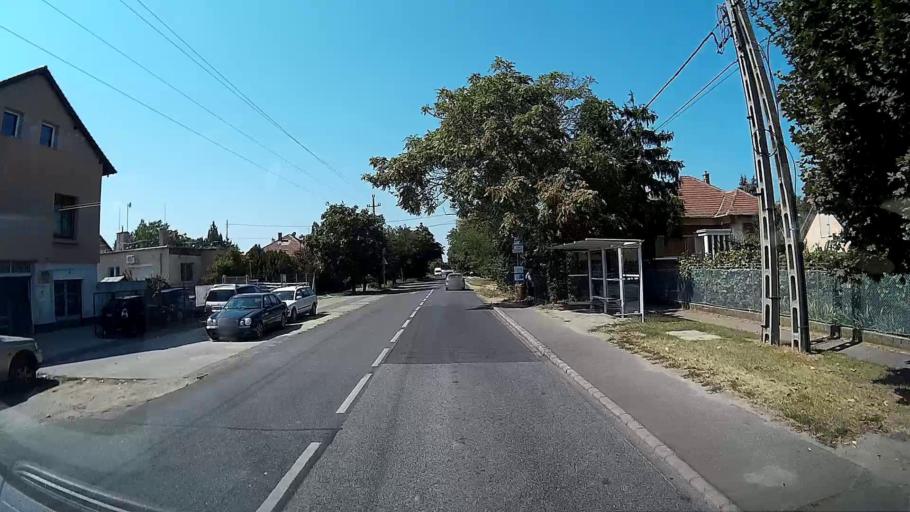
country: HU
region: Budapest
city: Budapest XVIII. keruelet
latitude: 47.4327
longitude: 19.1892
